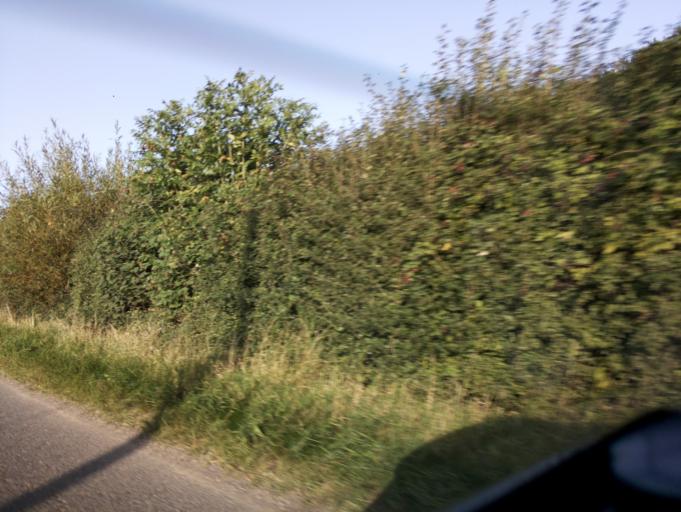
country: GB
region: England
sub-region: Gloucestershire
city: Gloucester
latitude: 51.9144
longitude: -2.2940
